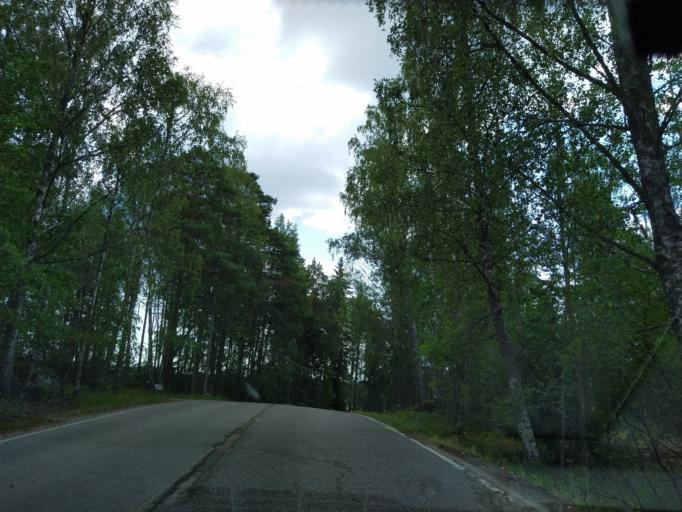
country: FI
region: Uusimaa
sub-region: Helsinki
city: Kirkkonummi
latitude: 60.0615
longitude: 24.4942
